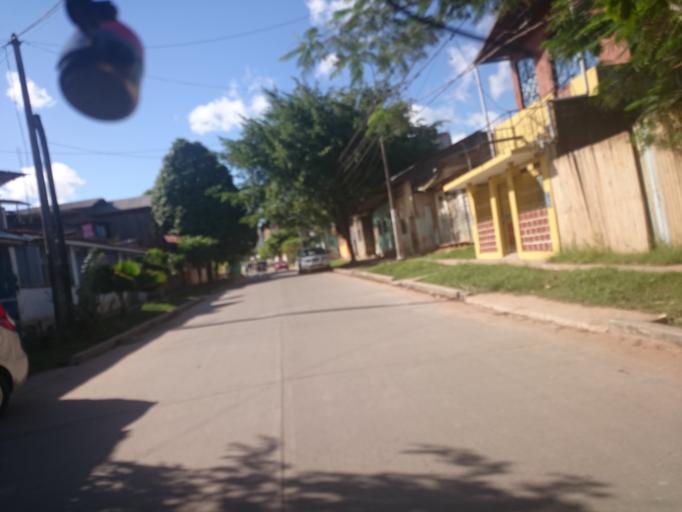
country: PE
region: Ucayali
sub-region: Provincia de Coronel Portillo
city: Pucallpa
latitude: -8.3840
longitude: -74.5379
